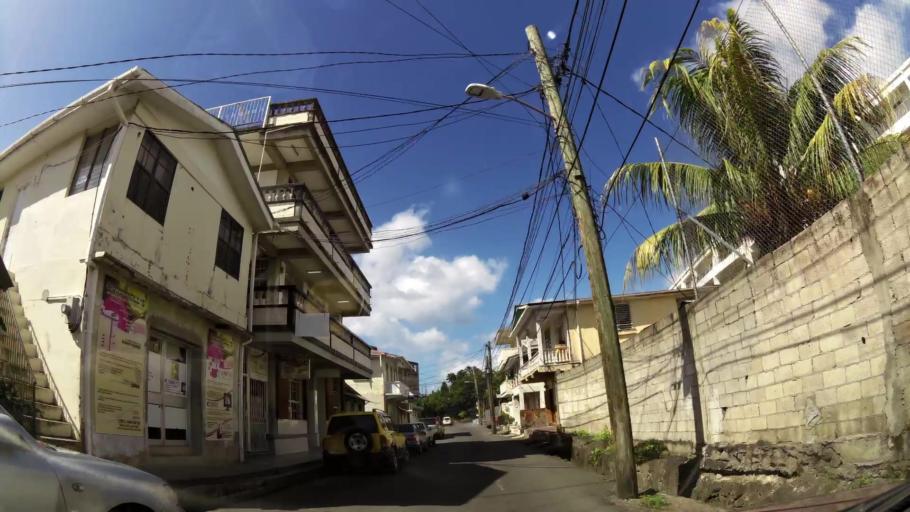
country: DM
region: Saint George
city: Roseau
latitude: 15.3009
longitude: -61.3852
